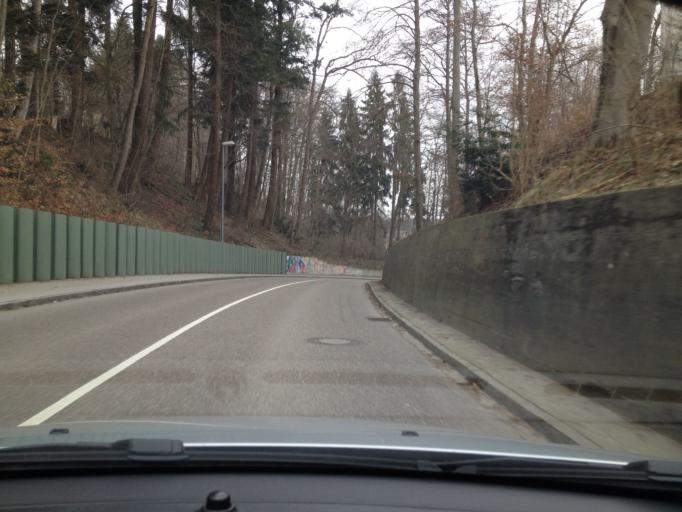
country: DE
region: Bavaria
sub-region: Swabia
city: Wehringen
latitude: 48.2731
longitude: 10.7881
